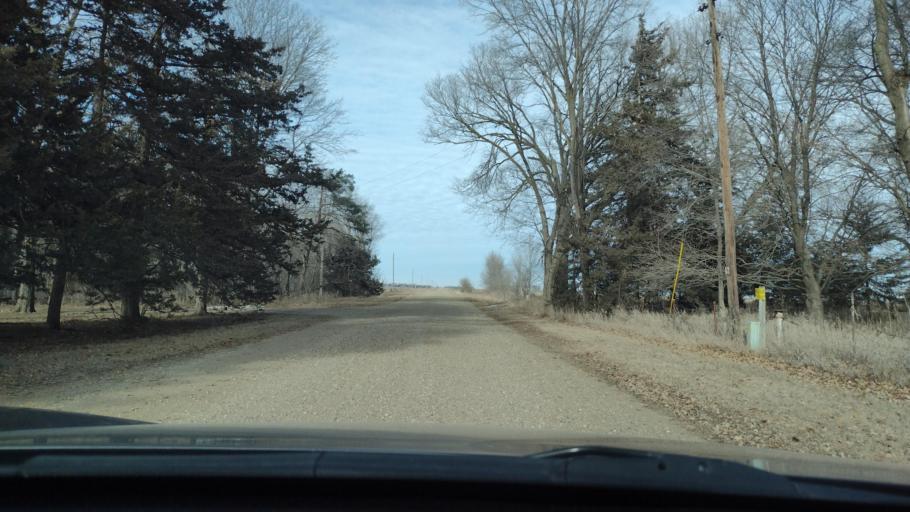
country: US
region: South Dakota
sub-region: Union County
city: Beresford
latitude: 42.9628
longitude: -96.8055
